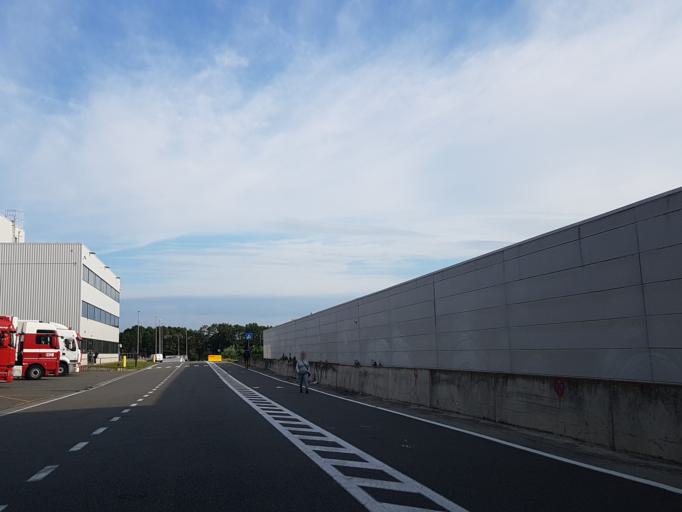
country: BE
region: Flanders
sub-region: Provincie Vlaams-Brabant
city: Machelen
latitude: 50.9036
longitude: 4.4485
